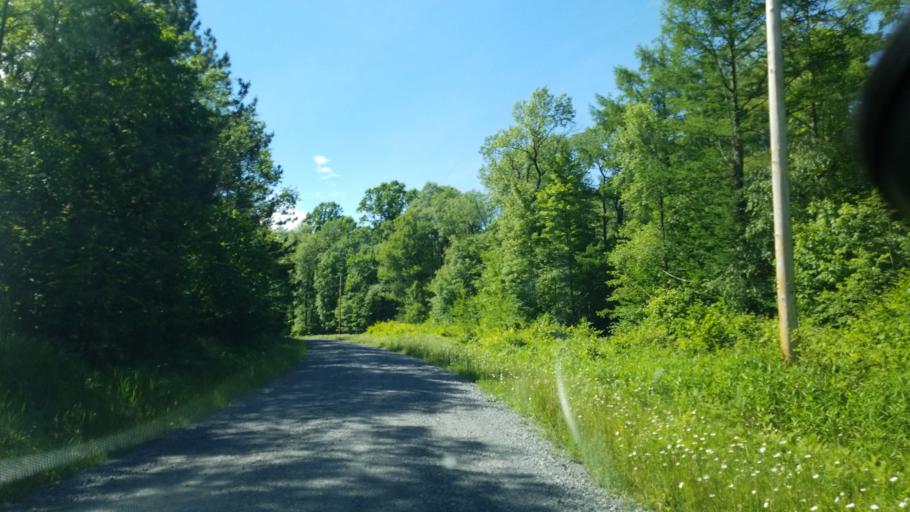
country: US
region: Pennsylvania
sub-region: Clearfield County
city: Clearfield
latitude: 41.1911
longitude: -78.4702
